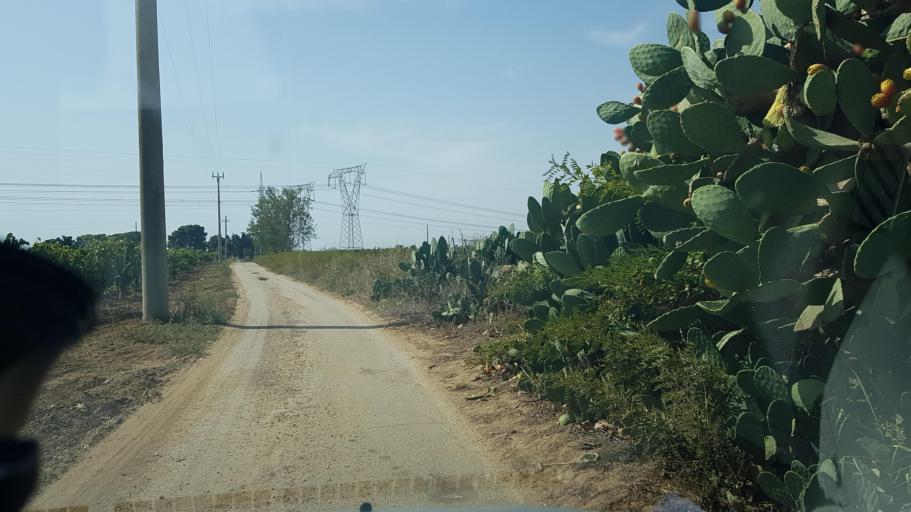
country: IT
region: Apulia
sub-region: Provincia di Brindisi
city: Brindisi
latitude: 40.6023
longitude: 17.8871
